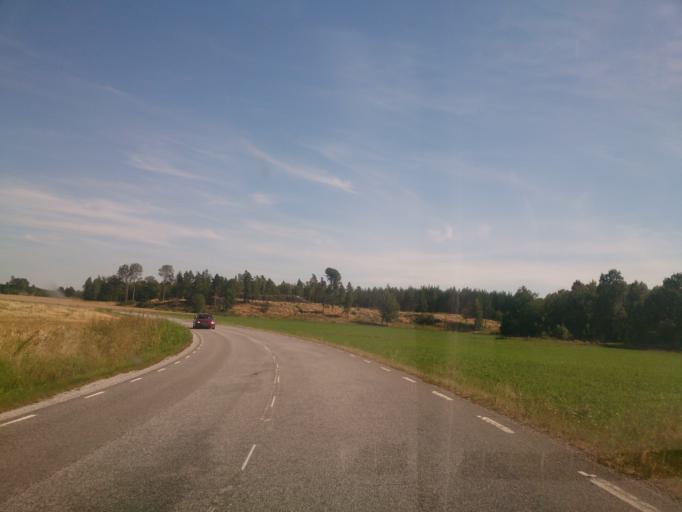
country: SE
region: OEstergoetland
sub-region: Norrkopings Kommun
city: Kimstad
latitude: 58.4802
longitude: 16.0118
